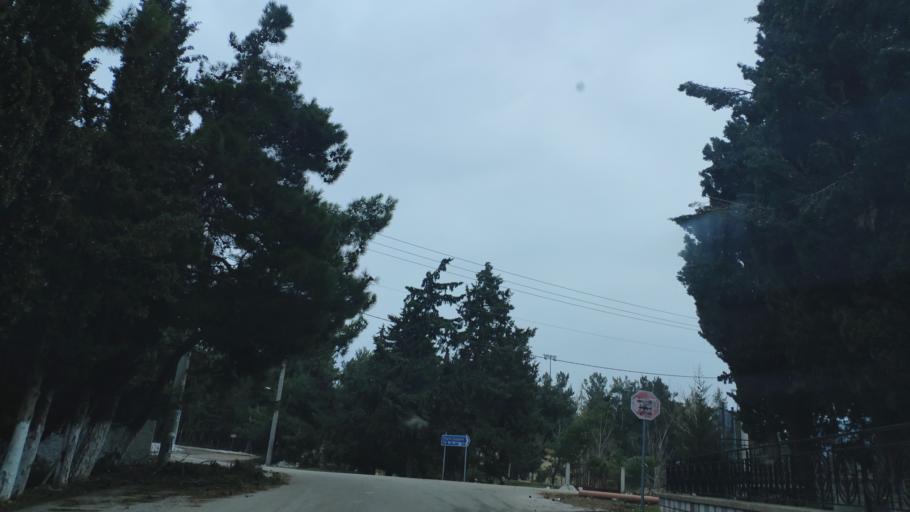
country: GR
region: Attica
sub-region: Nomarchia Dytikis Attikis
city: Vilia
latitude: 38.1655
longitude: 23.3418
